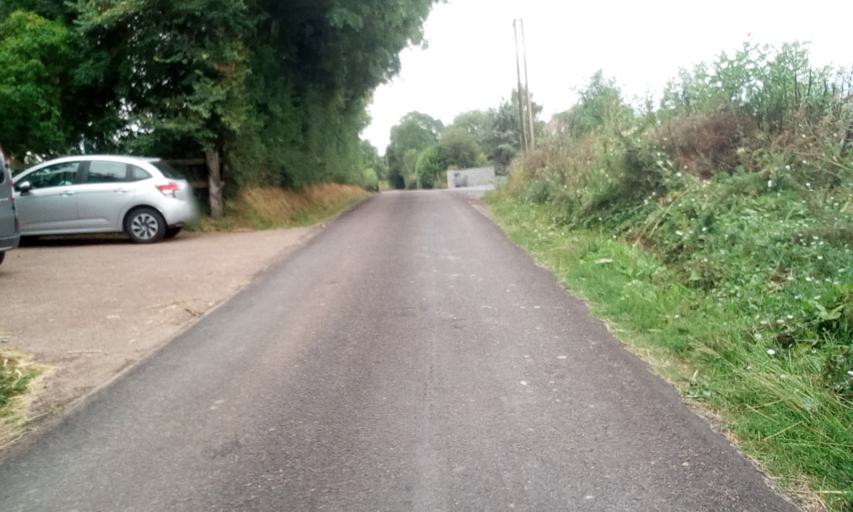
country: FR
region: Lower Normandy
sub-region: Departement du Calvados
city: Troarn
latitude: 49.1934
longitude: -0.1557
